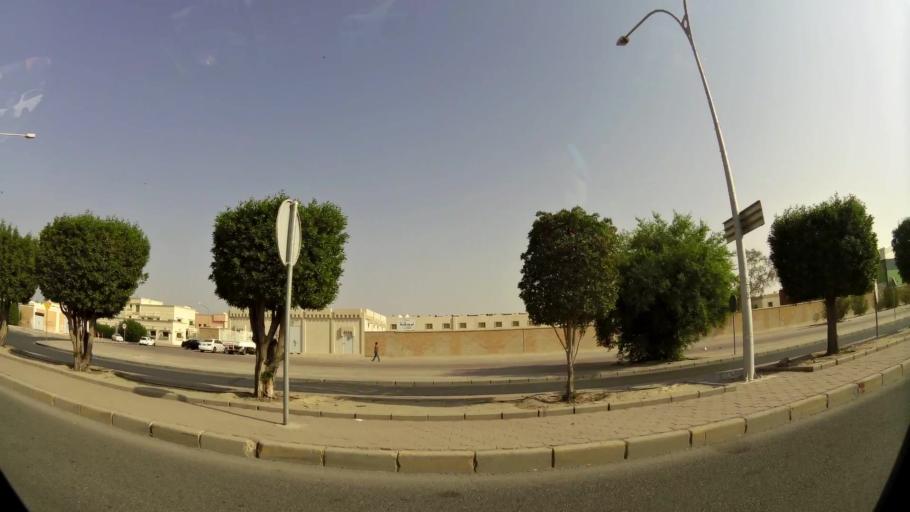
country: KW
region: Muhafazat al Jahra'
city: Al Jahra'
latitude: 29.3400
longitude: 47.7020
